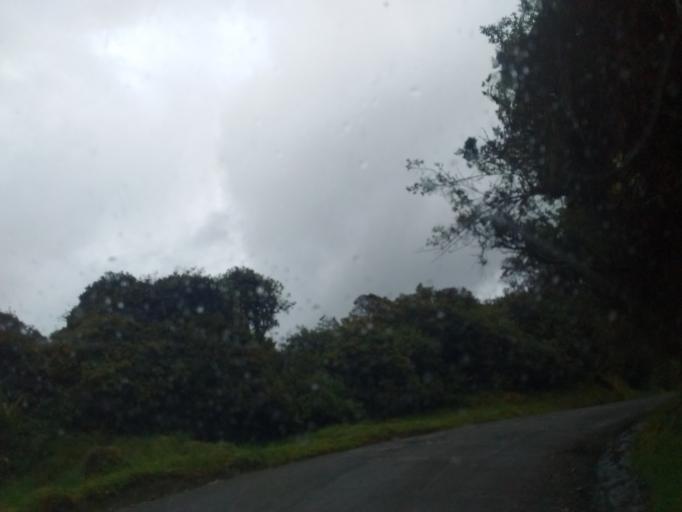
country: CO
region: Cauca
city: Totoro
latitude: 2.3474
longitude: -76.3081
